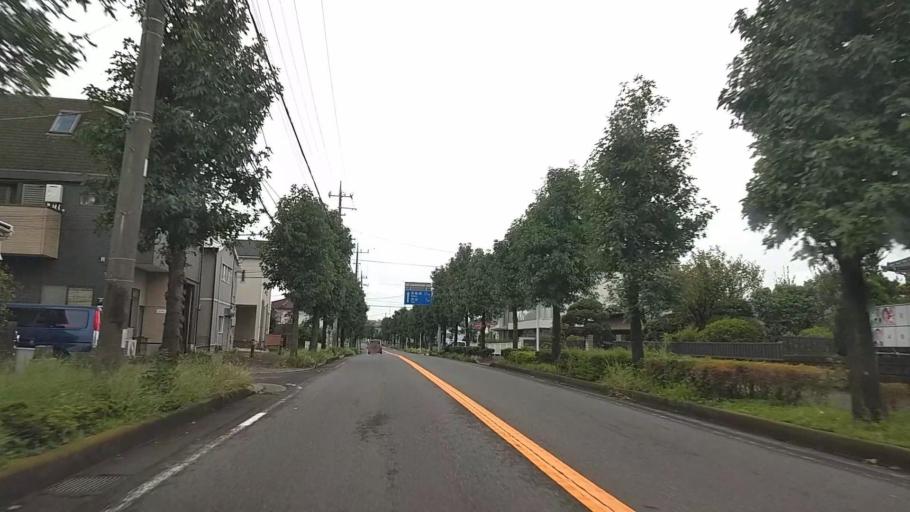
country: JP
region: Kanagawa
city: Fujisawa
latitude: 35.4147
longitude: 139.4751
